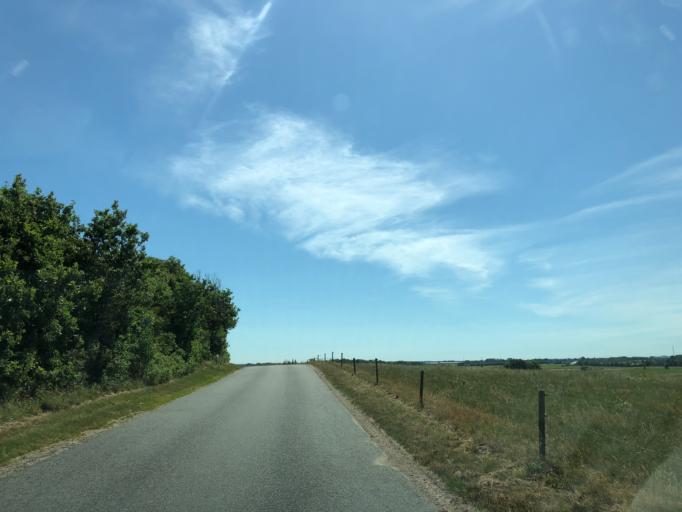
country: DK
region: Central Jutland
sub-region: Skive Kommune
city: Skive
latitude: 56.4847
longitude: 8.9991
